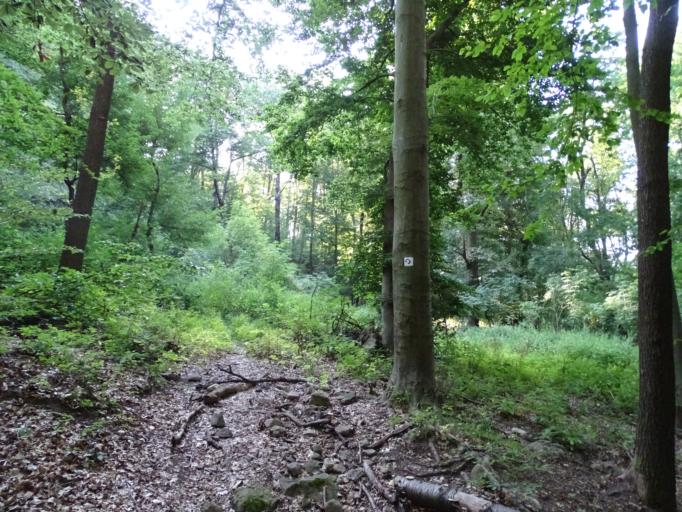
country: HU
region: Pest
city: Pilisszentkereszt
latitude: 47.7072
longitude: 18.8861
